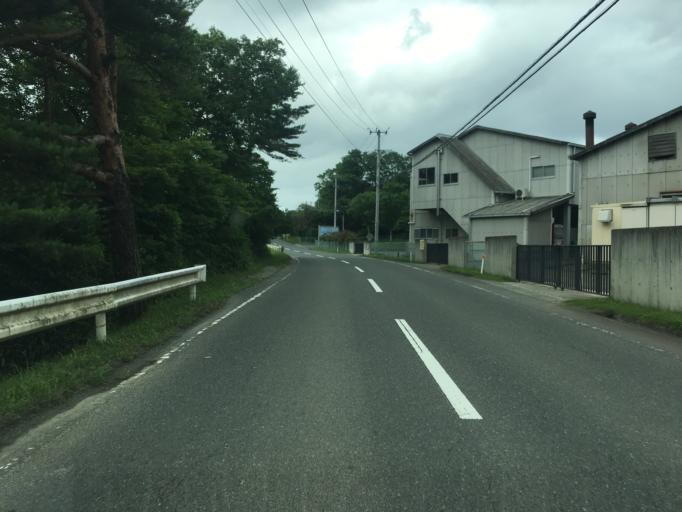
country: JP
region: Miyagi
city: Marumori
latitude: 37.7497
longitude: 140.9616
